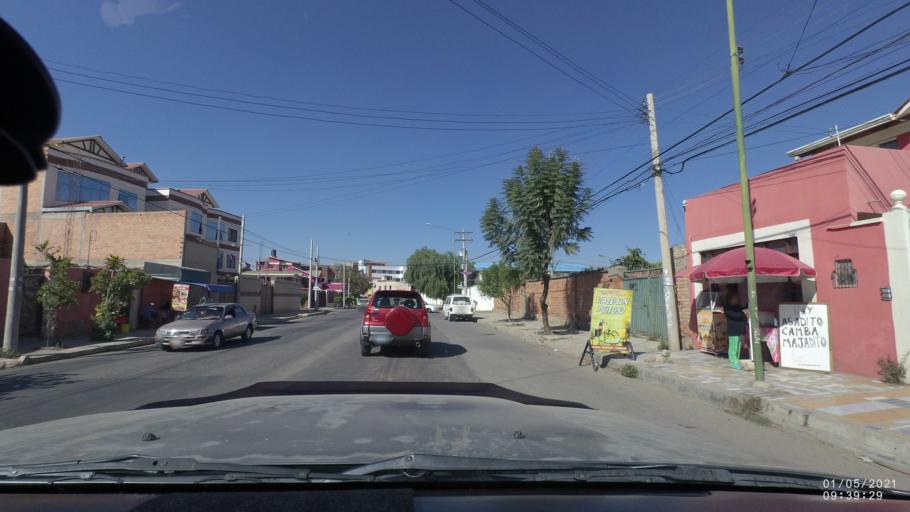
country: BO
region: Cochabamba
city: Cochabamba
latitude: -17.4140
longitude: -66.1691
